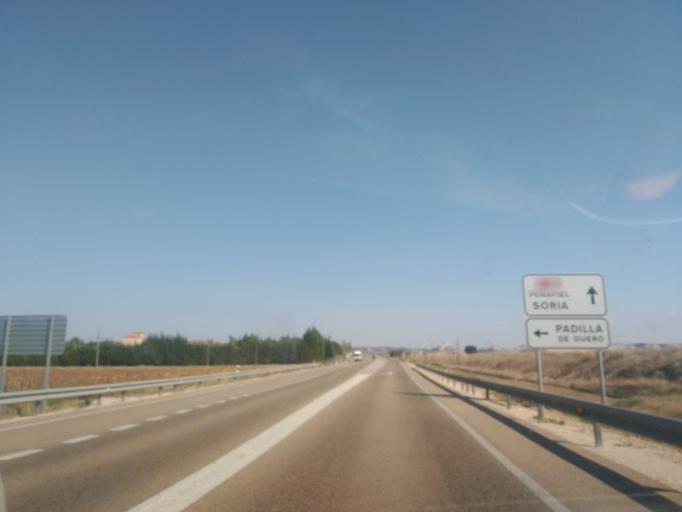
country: ES
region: Castille and Leon
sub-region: Provincia de Valladolid
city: Manzanillo
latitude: 41.6117
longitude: -4.1705
